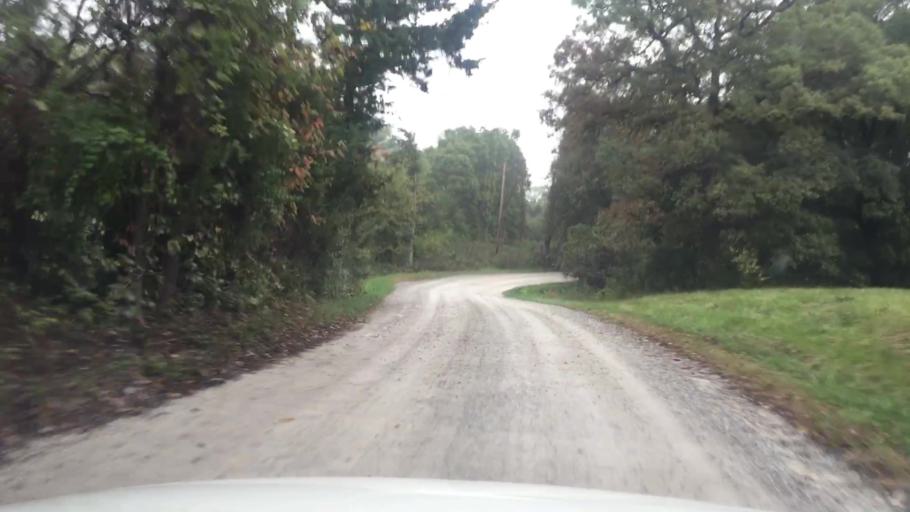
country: US
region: Missouri
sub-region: Boone County
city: Ashland
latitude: 38.8186
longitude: -92.2982
